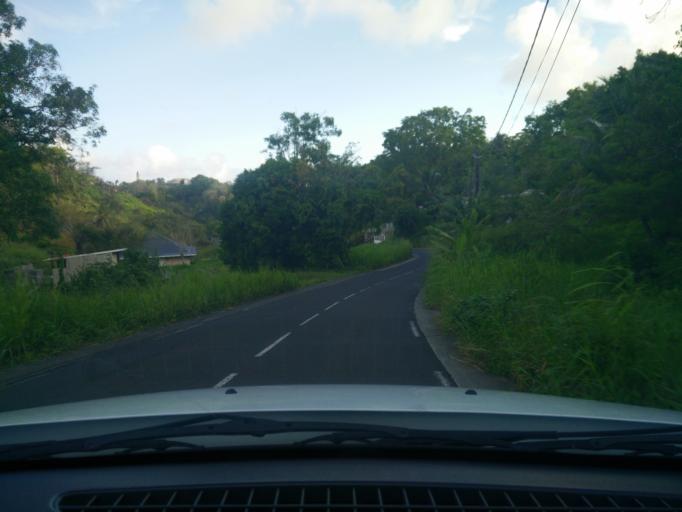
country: GP
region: Guadeloupe
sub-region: Guadeloupe
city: Les Abymes
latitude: 16.2460
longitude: -61.4921
